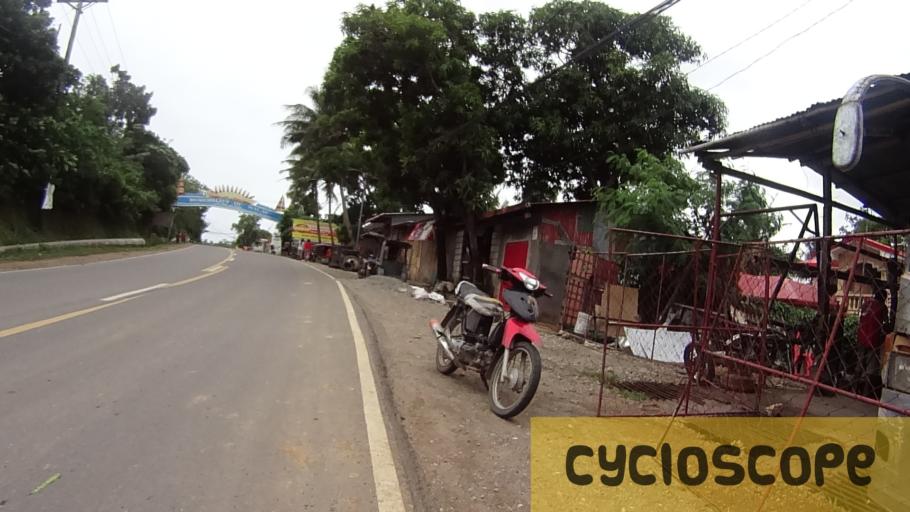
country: PH
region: Western Visayas
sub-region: Province of Aklan
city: Caticlan
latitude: 11.9328
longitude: 121.9585
